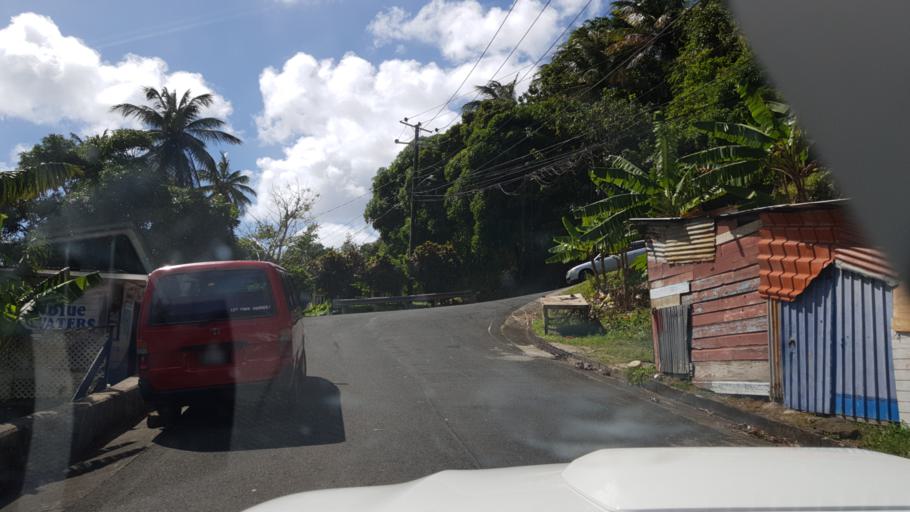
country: LC
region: Castries Quarter
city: Castries
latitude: 13.9845
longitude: -60.9723
